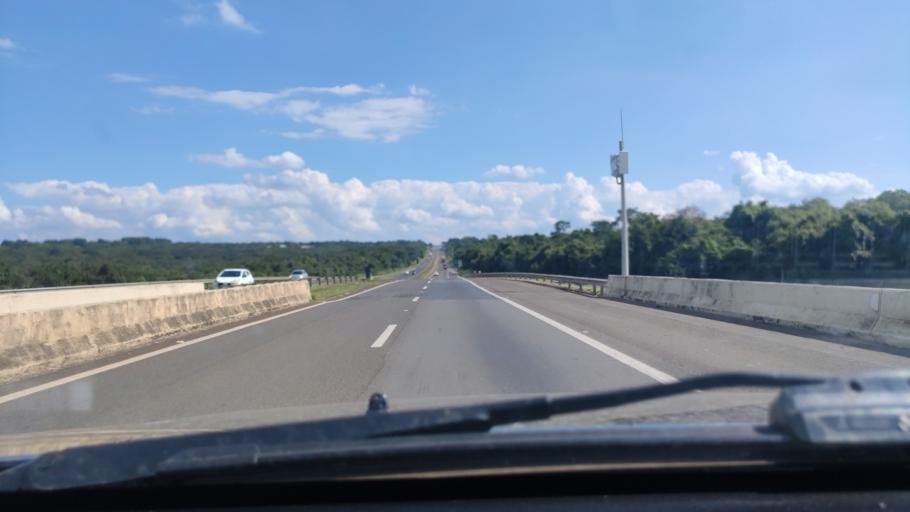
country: BR
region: Sao Paulo
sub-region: Bauru
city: Bauru
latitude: -22.3415
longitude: -49.0227
